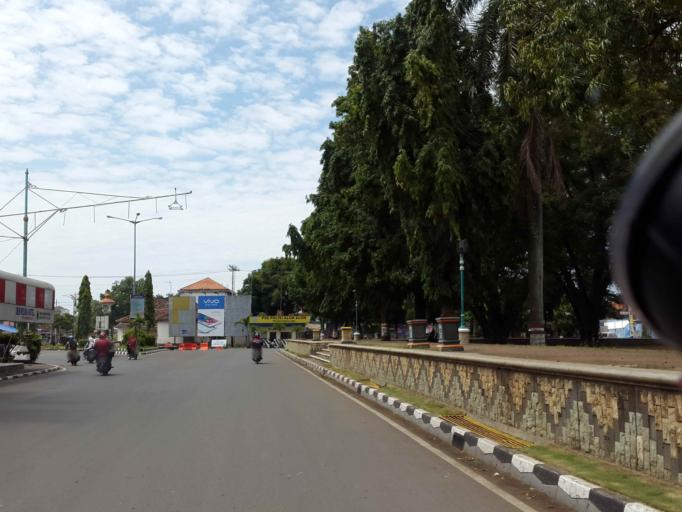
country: ID
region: Central Java
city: Pemalang
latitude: -6.8906
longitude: 109.3802
